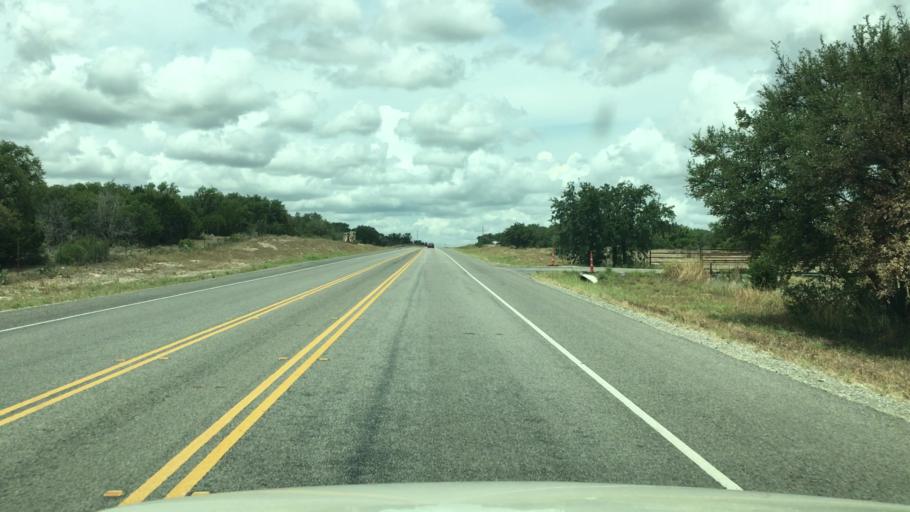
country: US
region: Texas
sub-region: McCulloch County
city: Brady
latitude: 31.0313
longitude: -99.2307
